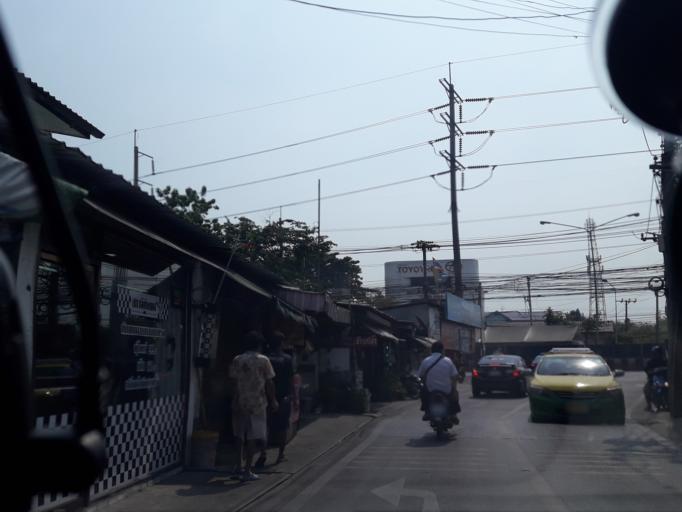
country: TH
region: Bangkok
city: Min Buri
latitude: 13.8134
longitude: 100.7063
